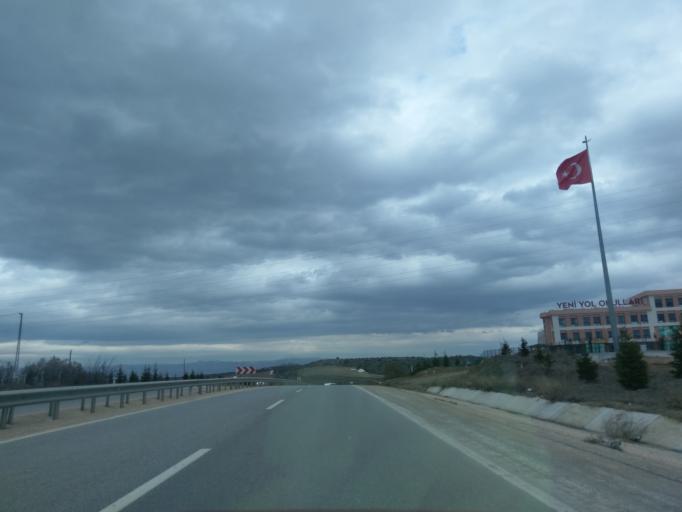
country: TR
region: Eskisehir
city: Eskisehir
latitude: 39.7404
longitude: 30.3929
